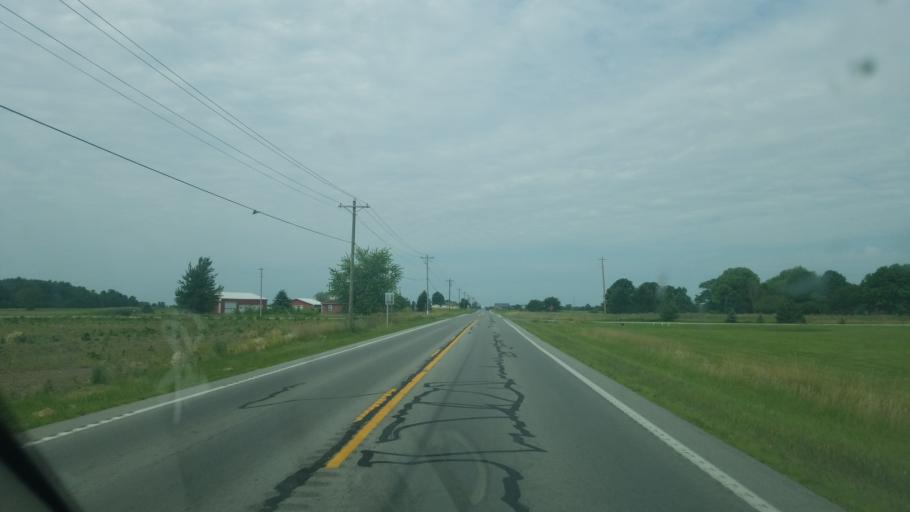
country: US
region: Ohio
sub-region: Seneca County
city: Fostoria
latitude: 41.0710
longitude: -83.4761
